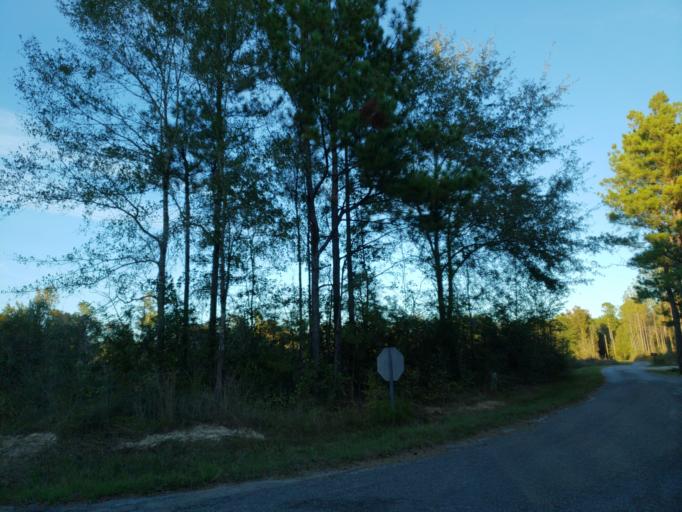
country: US
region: Mississippi
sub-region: Wayne County
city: Belmont
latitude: 31.4648
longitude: -88.5207
